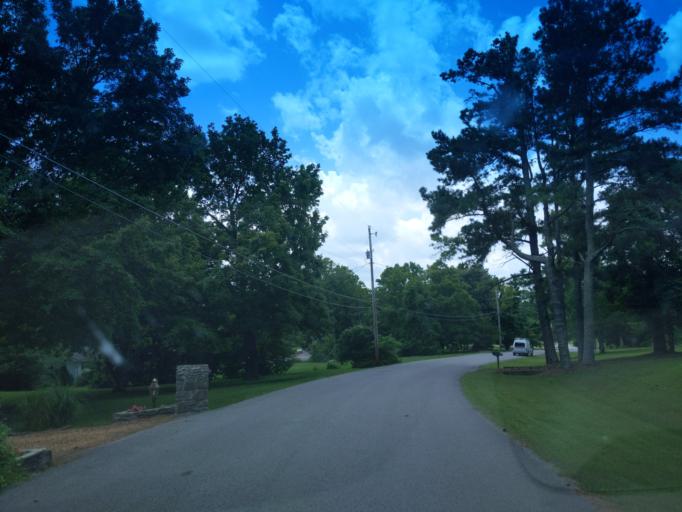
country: US
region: Tennessee
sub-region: Williamson County
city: Brentwood Estates
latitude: 36.0274
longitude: -86.7741
